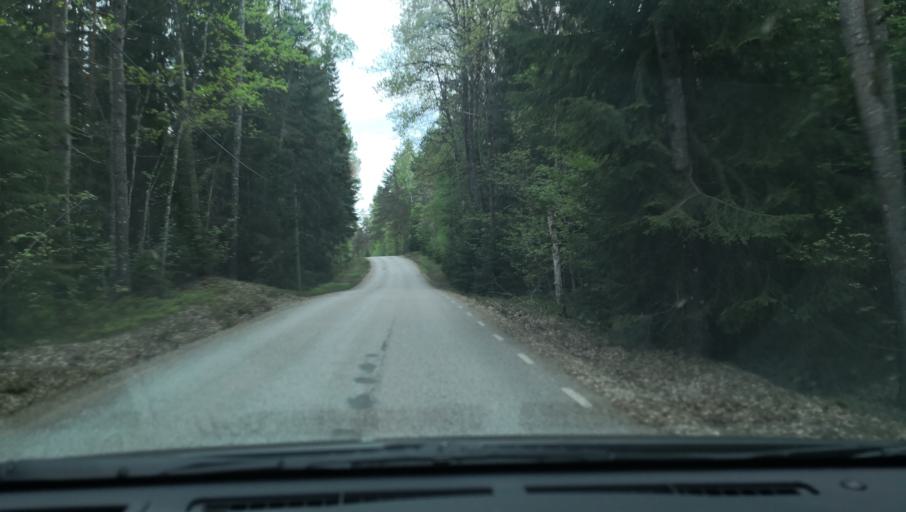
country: SE
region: Vaestmanland
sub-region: Skinnskattebergs Kommun
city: Skinnskatteberg
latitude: 59.8263
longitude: 15.5531
